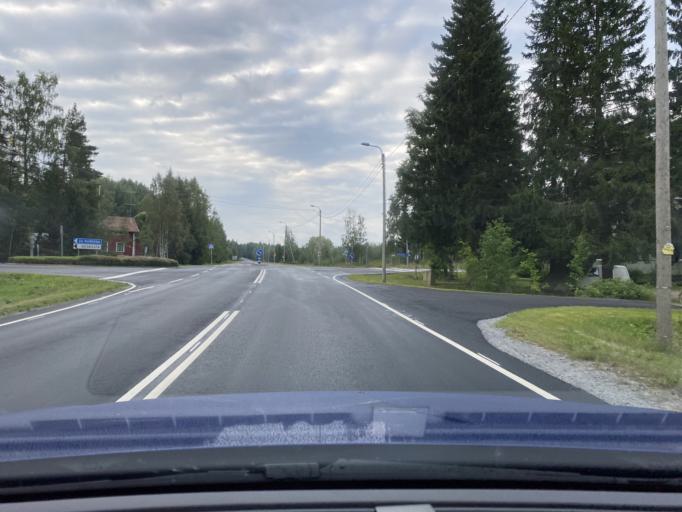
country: FI
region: Southern Ostrobothnia
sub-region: Seinaejoki
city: Jurva
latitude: 62.6831
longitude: 21.9717
